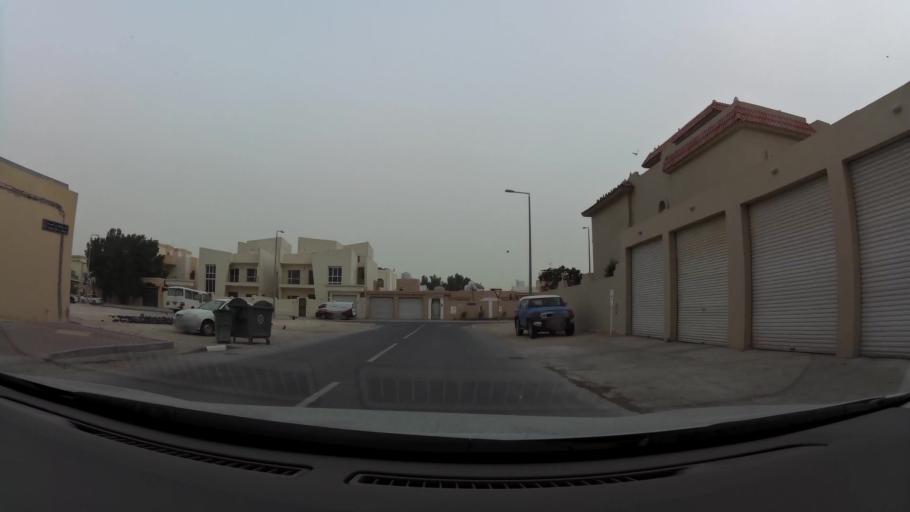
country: QA
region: Baladiyat ad Dawhah
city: Doha
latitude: 25.2494
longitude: 51.4792
